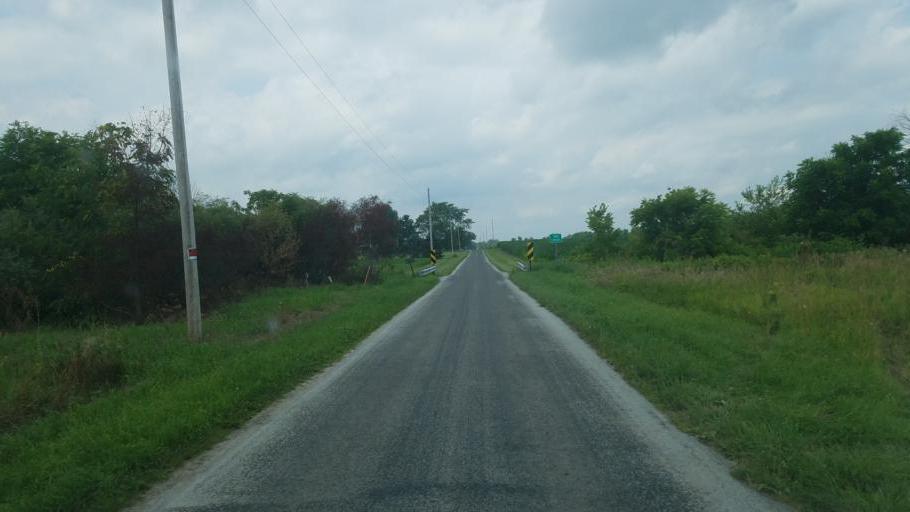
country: US
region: Ohio
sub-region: Hardin County
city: Kenton
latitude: 40.5890
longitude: -83.5288
